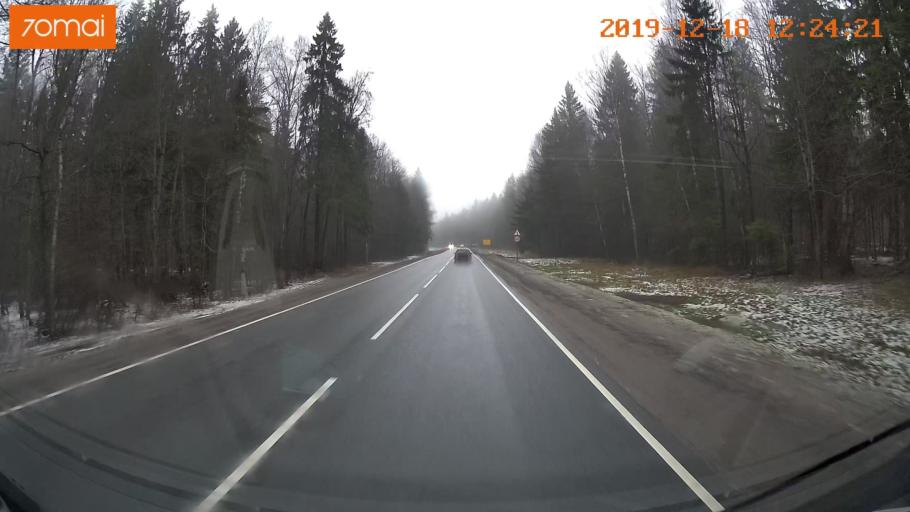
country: RU
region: Moskovskaya
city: Novopetrovskoye
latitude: 56.0237
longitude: 36.5003
